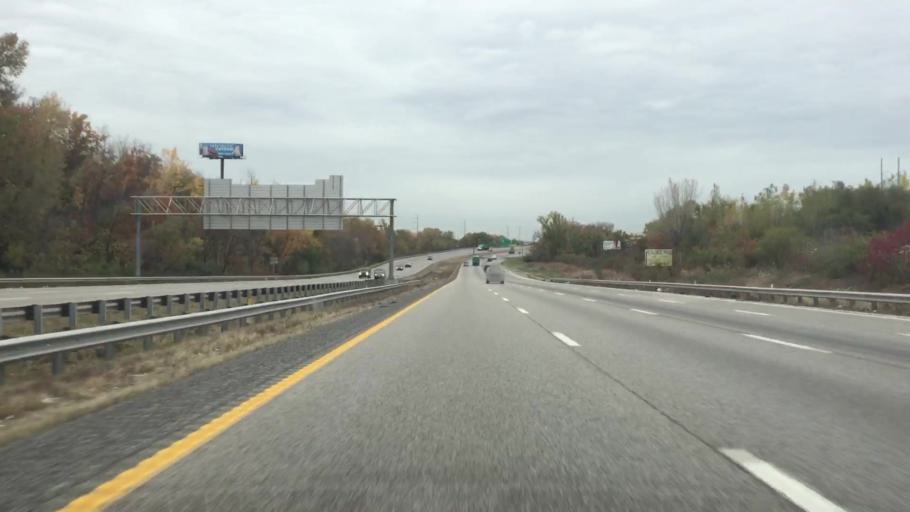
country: US
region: Missouri
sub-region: Jackson County
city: Sugar Creek
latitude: 39.0752
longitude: -94.4893
